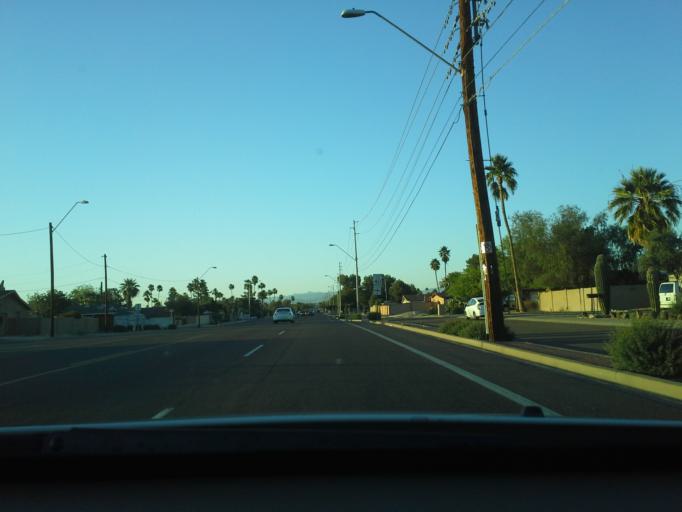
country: US
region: Arizona
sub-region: Maricopa County
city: Paradise Valley
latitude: 33.5844
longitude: -111.9957
